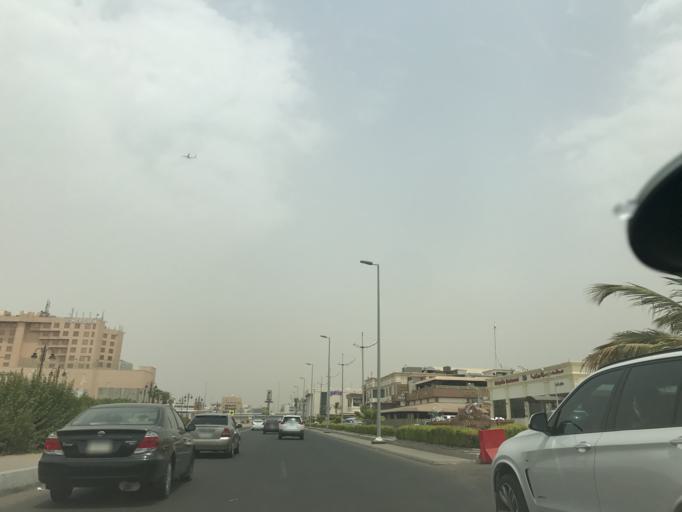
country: SA
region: Makkah
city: Jeddah
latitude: 21.5573
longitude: 39.1700
